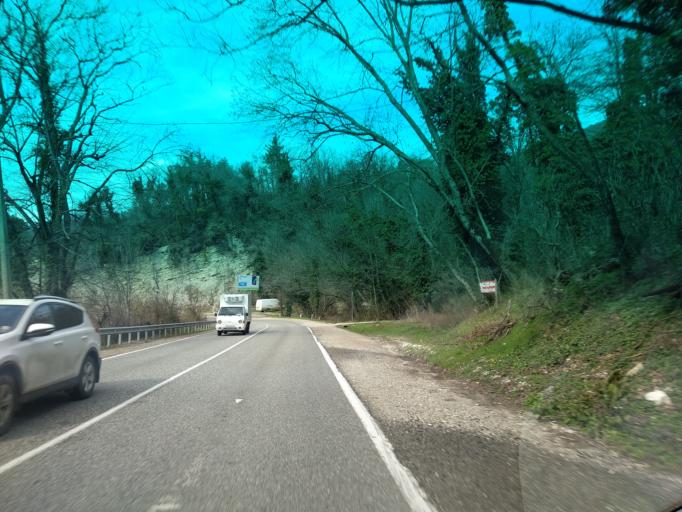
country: RU
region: Krasnodarskiy
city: Shepsi
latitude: 44.0798
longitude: 39.1343
